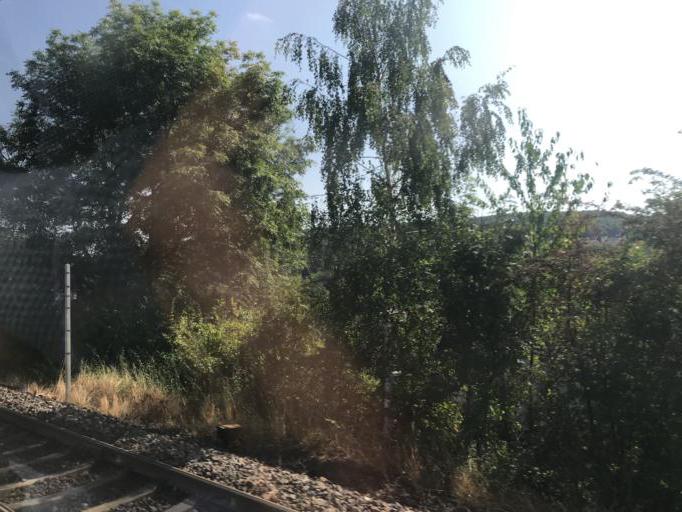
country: DE
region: Saarland
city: Sulzbach
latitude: 49.2843
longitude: 7.0369
